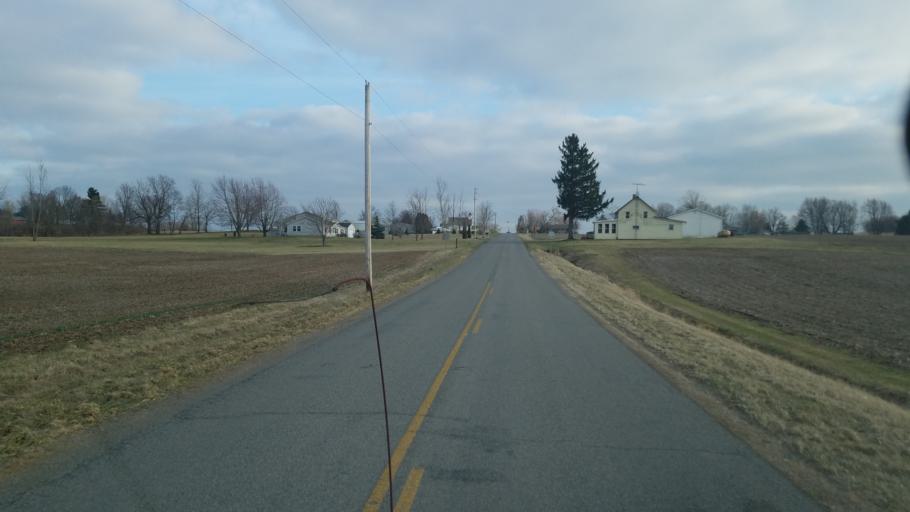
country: US
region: Ohio
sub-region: Logan County
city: West Liberty
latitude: 40.3030
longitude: -83.6616
